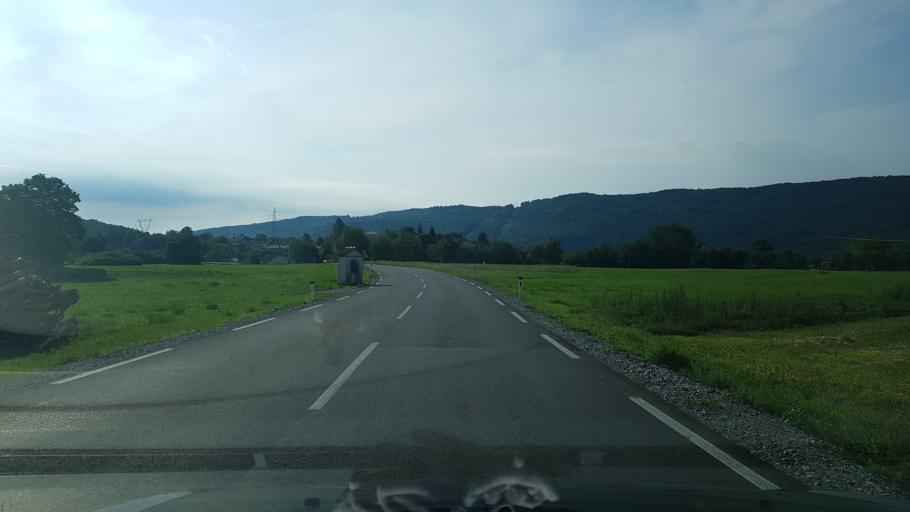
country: SI
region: Divaca
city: Divaca
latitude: 45.6610
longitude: 14.0237
